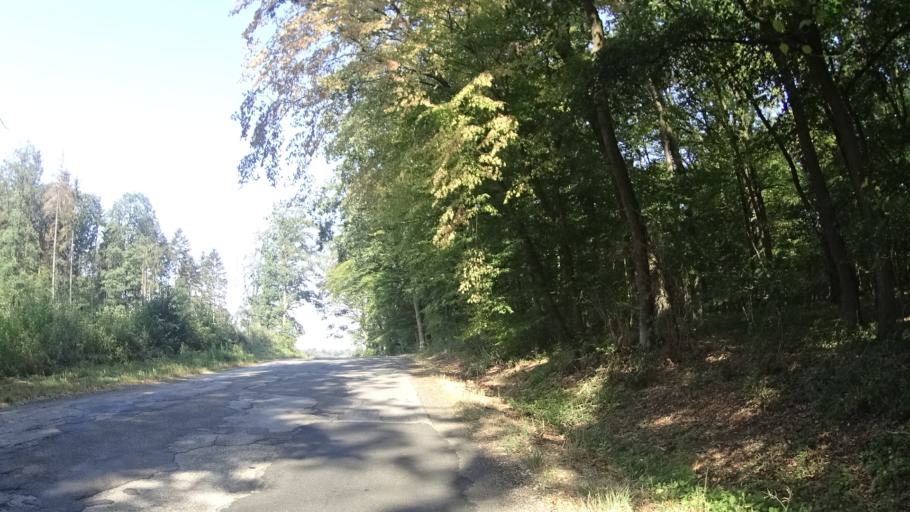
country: CZ
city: Smidary
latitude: 50.2798
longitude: 15.5296
